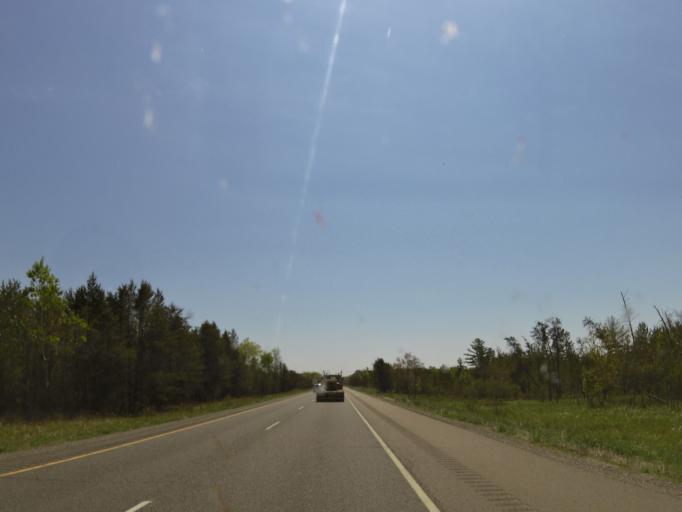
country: US
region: Wisconsin
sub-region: Jackson County
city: Black River Falls
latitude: 44.2653
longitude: -90.7781
